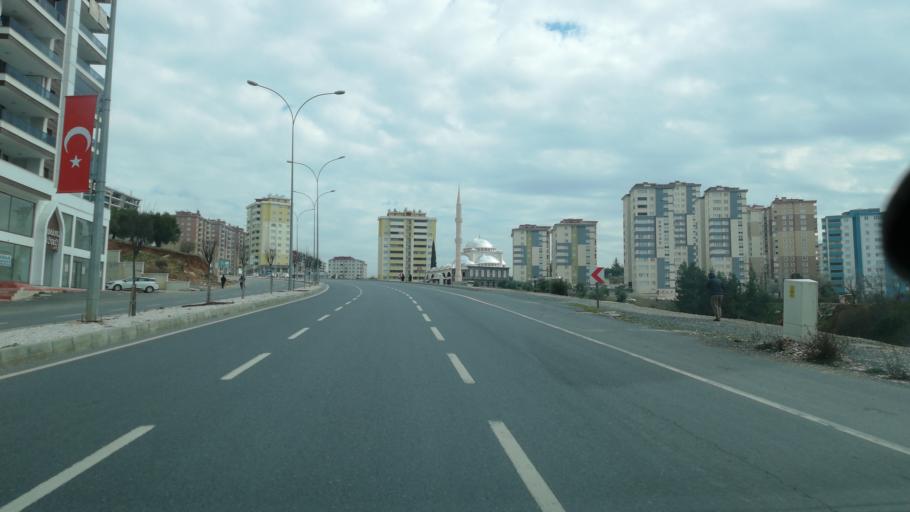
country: TR
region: Kahramanmaras
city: Kahramanmaras
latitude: 37.5852
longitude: 36.8576
